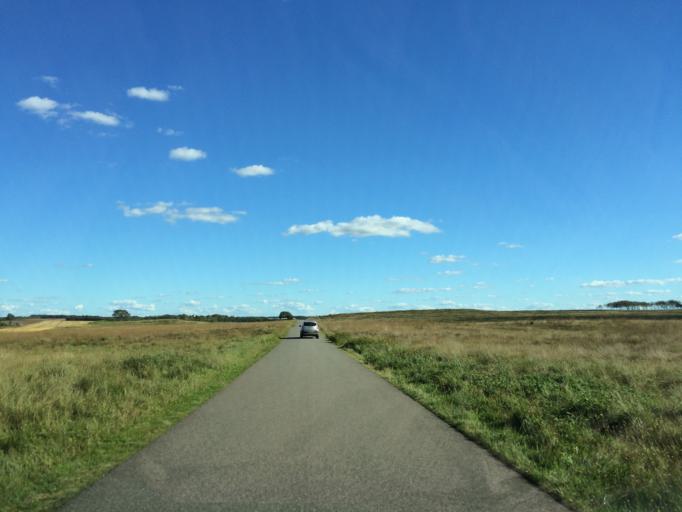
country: DK
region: Central Jutland
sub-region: Holstebro Kommune
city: Holstebro
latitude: 56.2708
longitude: 8.5139
